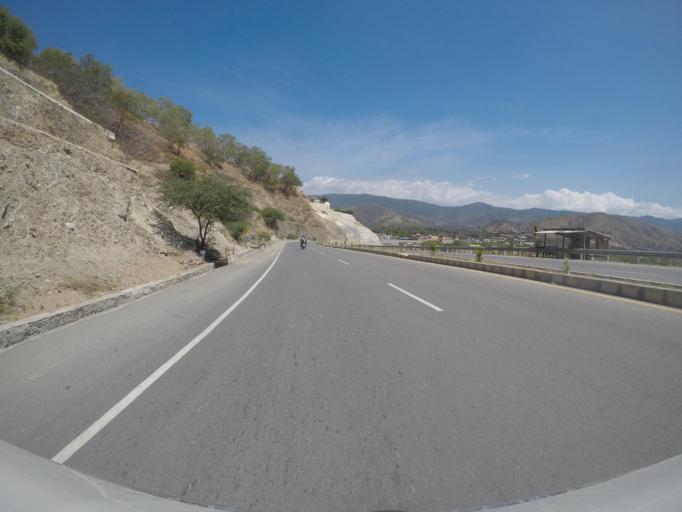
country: TL
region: Dili
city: Dili
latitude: -8.5648
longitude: 125.4913
